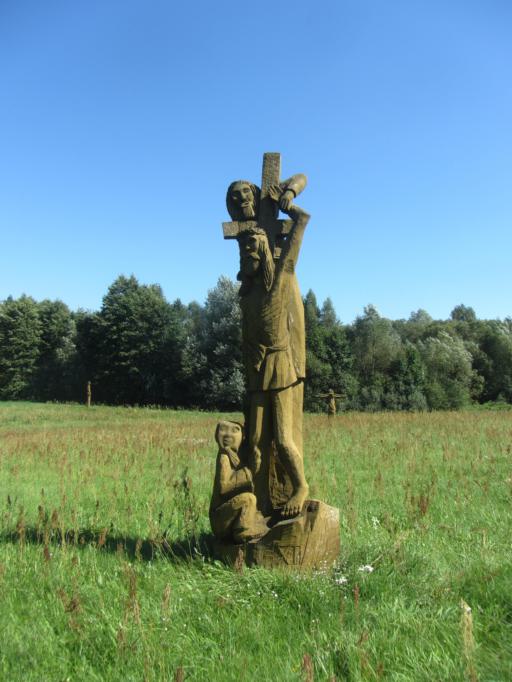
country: LT
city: Simnas
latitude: 54.2612
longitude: 23.6953
